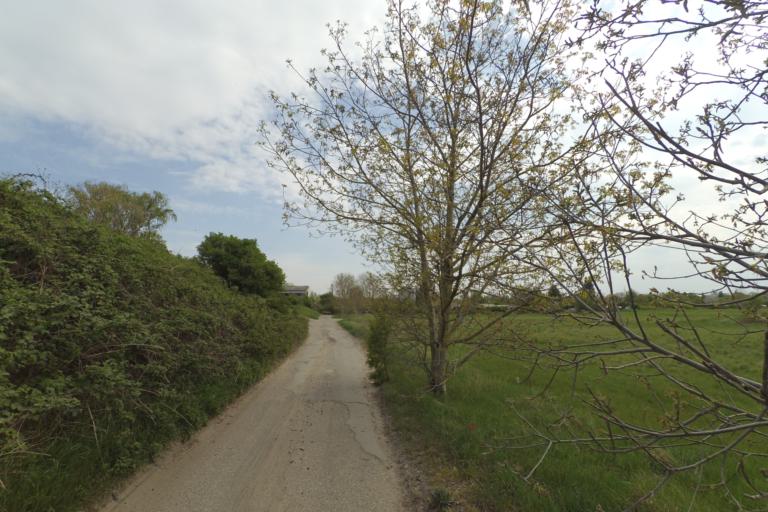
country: DE
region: Baden-Wuerttemberg
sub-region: Karlsruhe Region
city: Mannheim
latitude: 49.5158
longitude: 8.4507
